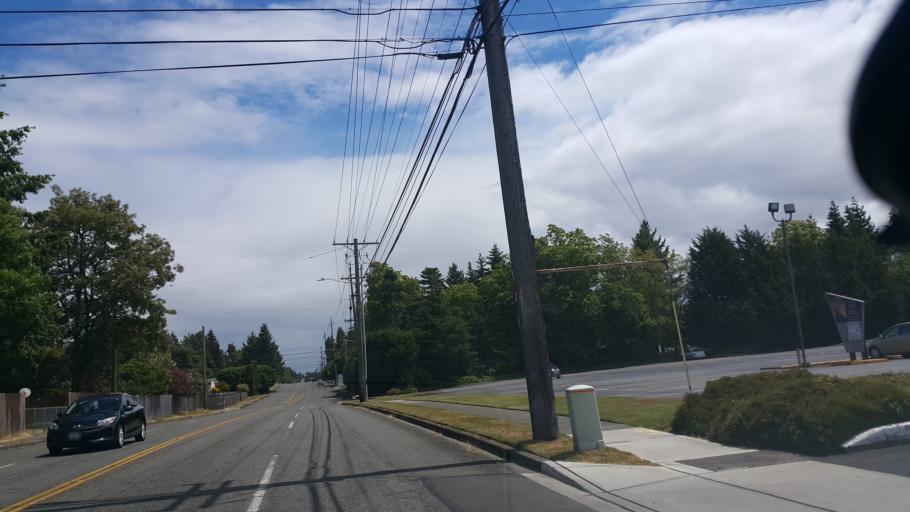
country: US
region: Washington
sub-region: Pierce County
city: Fircrest
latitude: 47.2499
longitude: -122.5327
